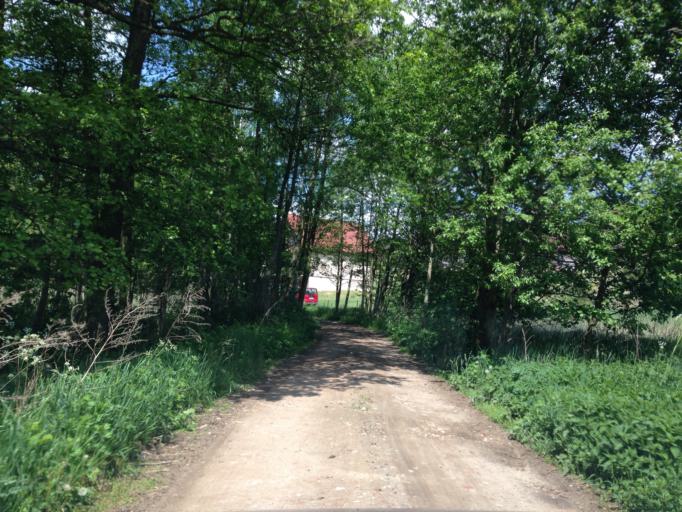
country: PL
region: Kujawsko-Pomorskie
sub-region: Powiat brodnicki
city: Brodnica
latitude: 53.3246
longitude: 19.3635
